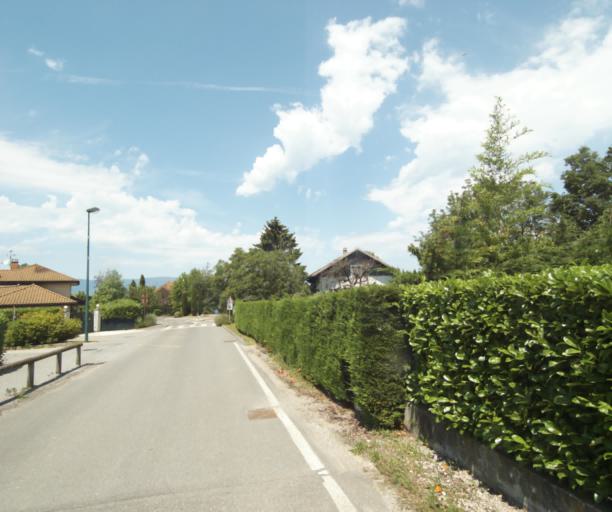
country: FR
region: Rhone-Alpes
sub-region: Departement de la Haute-Savoie
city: Messery
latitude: 46.3659
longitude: 6.3240
